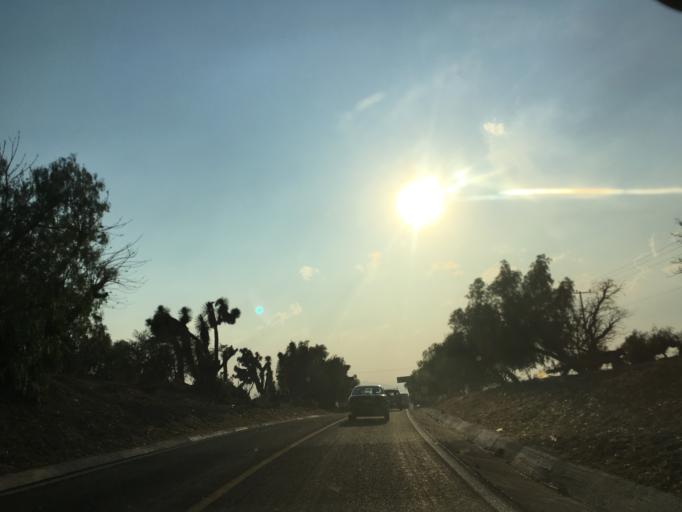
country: MX
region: Michoacan
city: Charo
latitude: 19.7465
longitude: -101.0527
